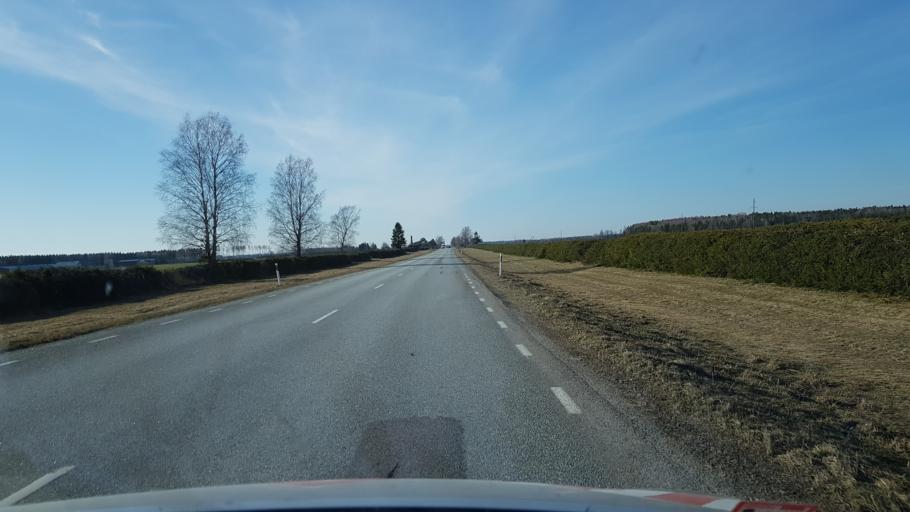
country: EE
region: Laeaene-Virumaa
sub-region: Vinni vald
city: Vinni
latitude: 59.2153
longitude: 26.5410
